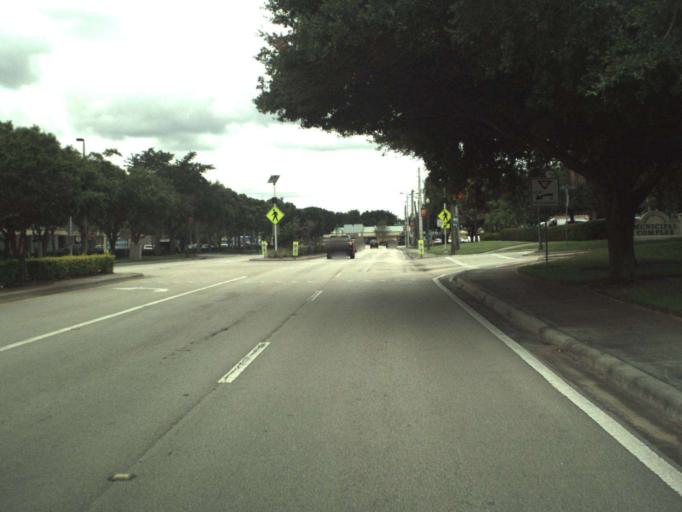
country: US
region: Florida
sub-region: Saint Lucie County
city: Port Saint Lucie
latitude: 27.2755
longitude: -80.3421
